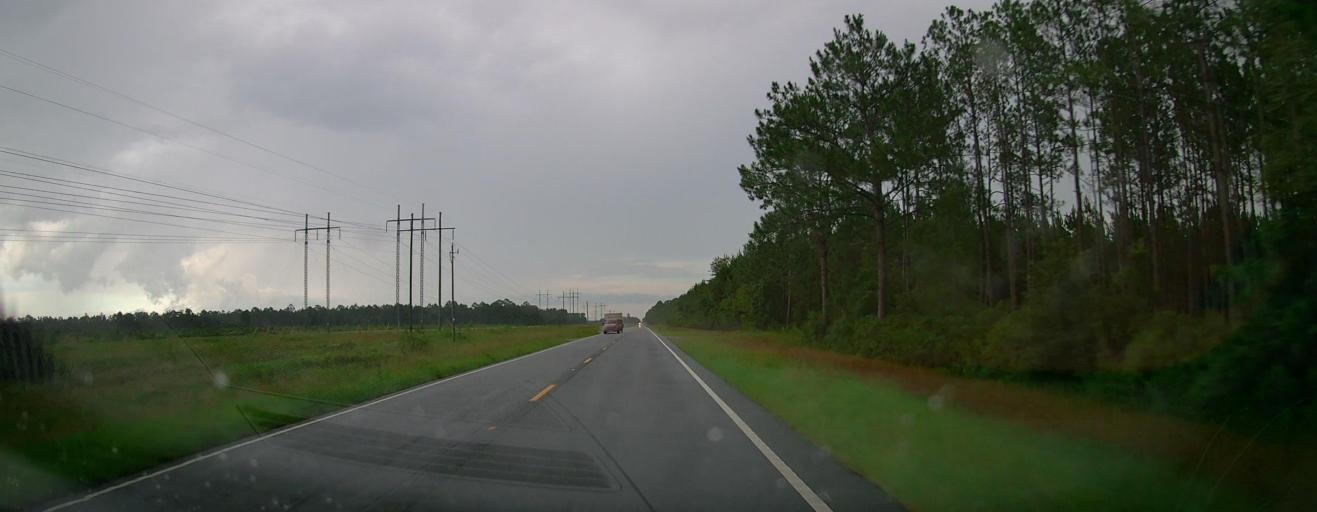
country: US
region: Georgia
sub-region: Brantley County
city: Nahunta
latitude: 31.3381
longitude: -81.8590
